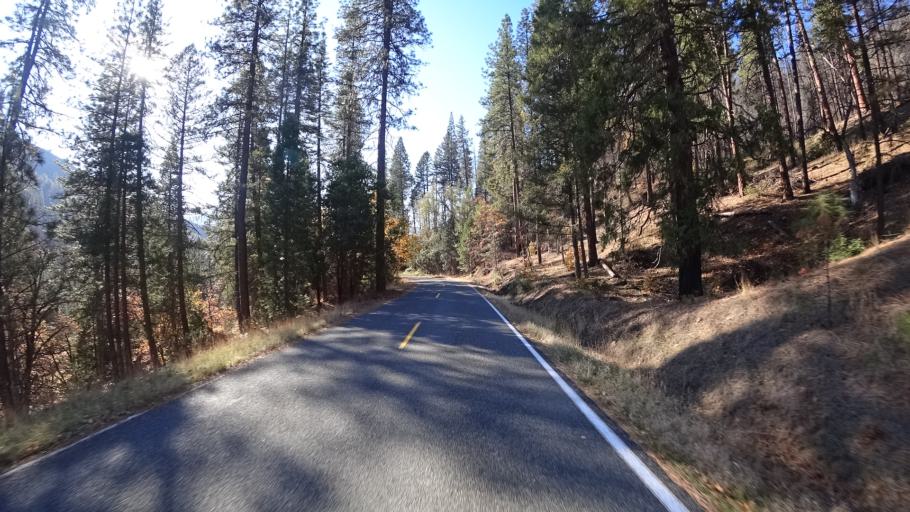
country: US
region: California
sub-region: Siskiyou County
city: Yreka
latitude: 41.8889
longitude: -122.8235
